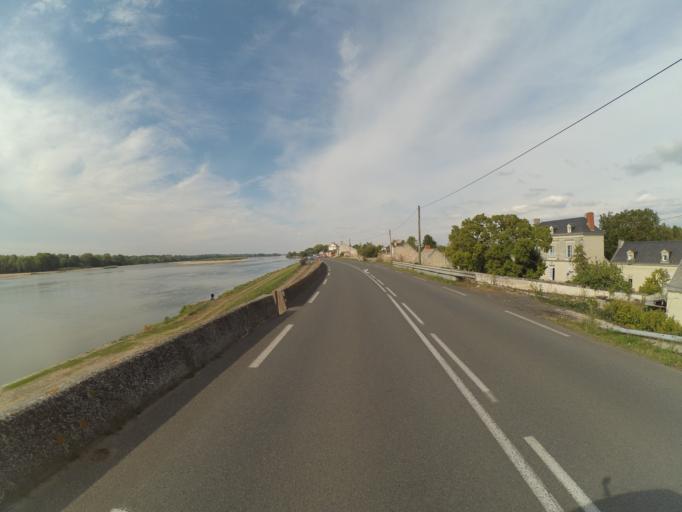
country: FR
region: Pays de la Loire
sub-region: Departement de Maine-et-Loire
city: Varennes-sur-Loire
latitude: 47.2310
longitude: 0.0398
